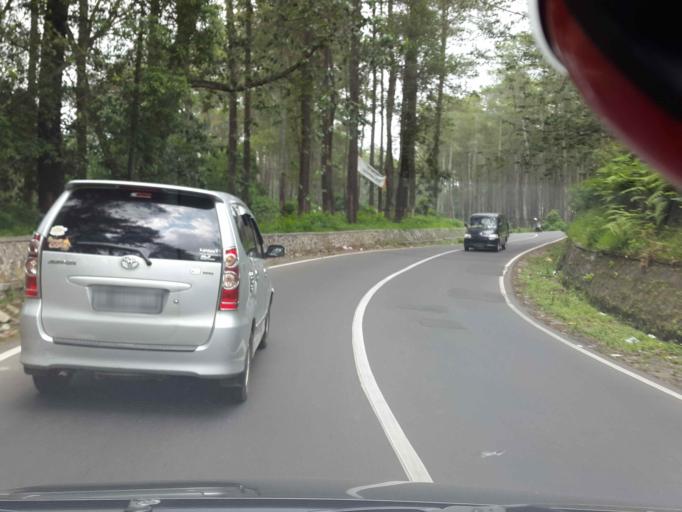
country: ID
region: West Java
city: Lembang
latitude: -6.7822
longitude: 107.6487
